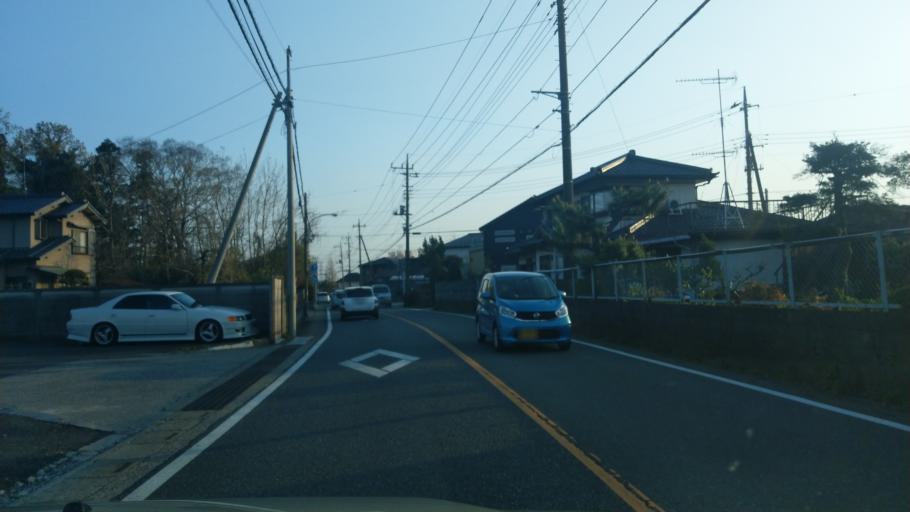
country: JP
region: Saitama
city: Ageoshimo
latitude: 36.0023
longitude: 139.6046
